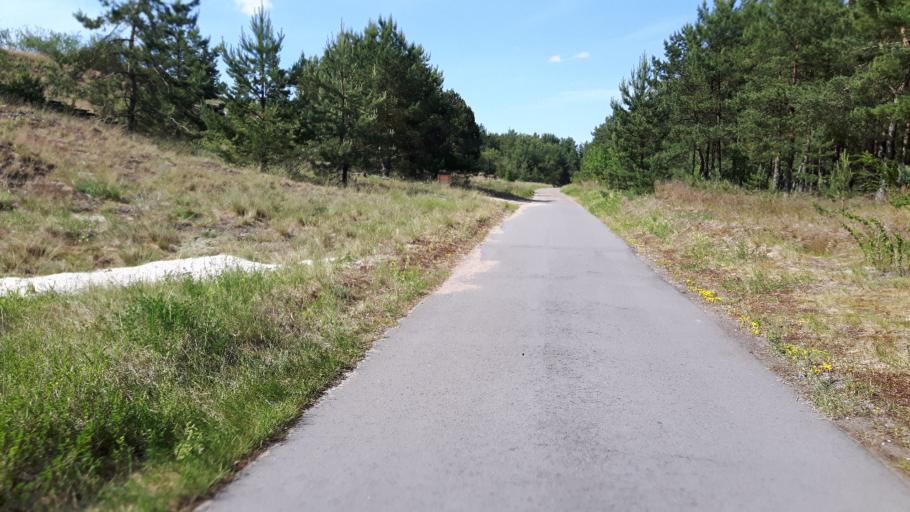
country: LT
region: Klaipedos apskritis
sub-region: Klaipeda
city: Klaipeda
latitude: 55.6950
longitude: 21.1020
